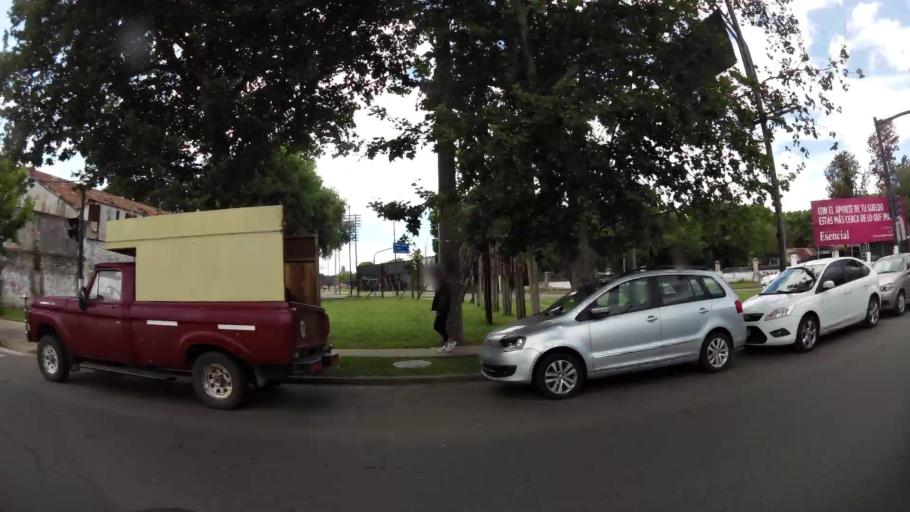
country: AR
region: Santa Fe
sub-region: Departamento de Rosario
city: Rosario
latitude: -32.9691
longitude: -60.6422
